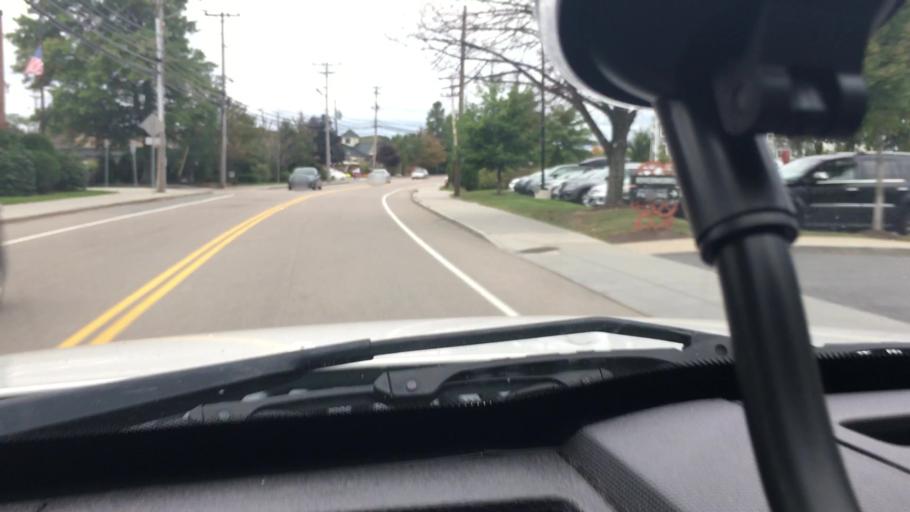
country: US
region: Massachusetts
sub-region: Middlesex County
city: Watertown
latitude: 42.3663
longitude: -71.2082
